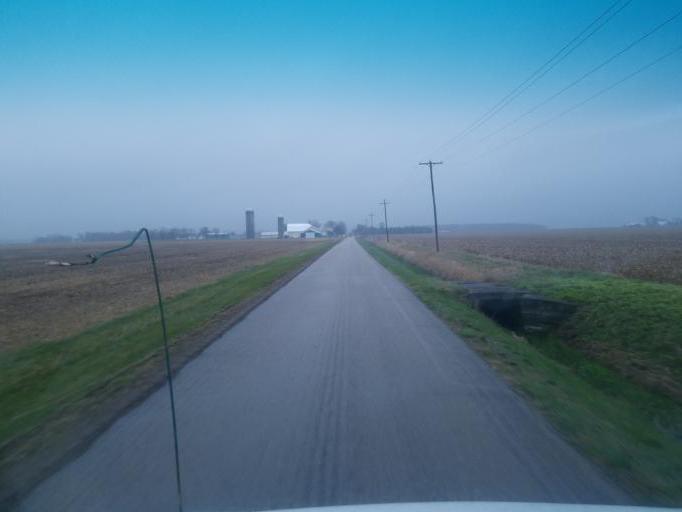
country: US
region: Ohio
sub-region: Fulton County
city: Archbold
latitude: 41.4278
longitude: -84.2615
